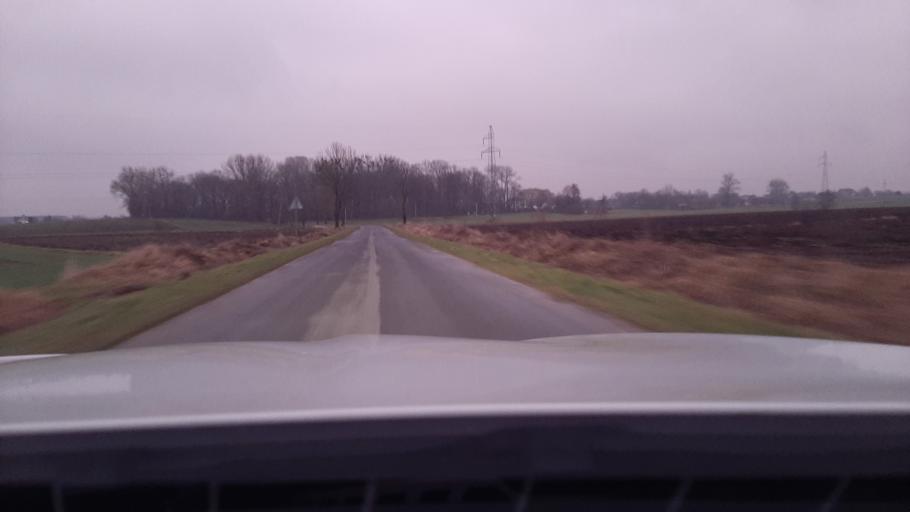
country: PL
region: Lublin Voivodeship
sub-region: Powiat lubelski
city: Garbow
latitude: 51.3502
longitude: 22.3820
